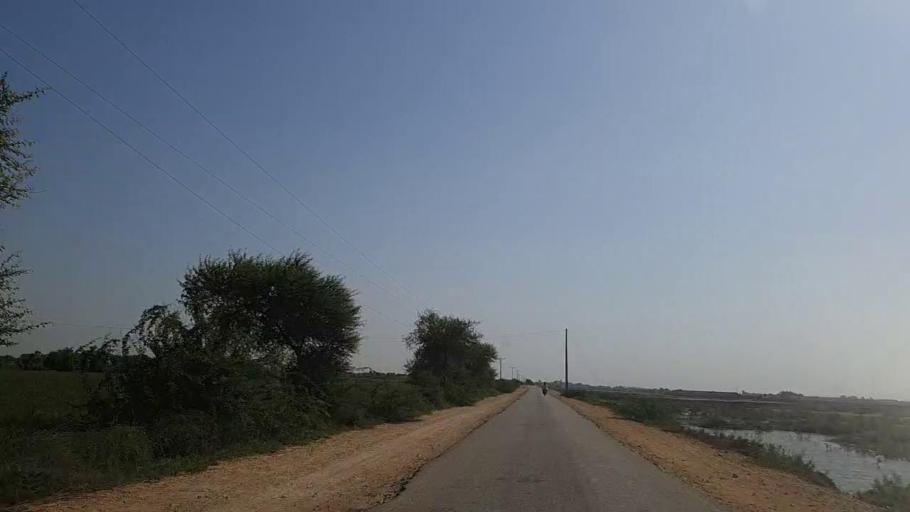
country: PK
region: Sindh
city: Mirpur Batoro
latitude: 24.6330
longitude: 68.2926
